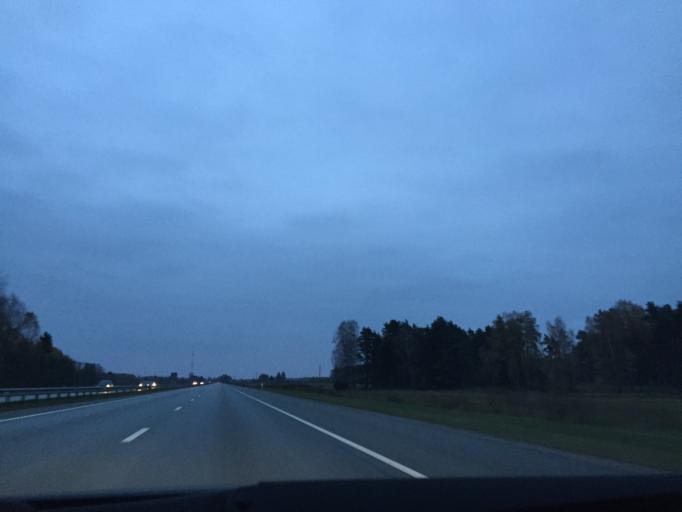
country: LV
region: Olaine
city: Olaine
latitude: 56.8081
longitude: 23.9961
